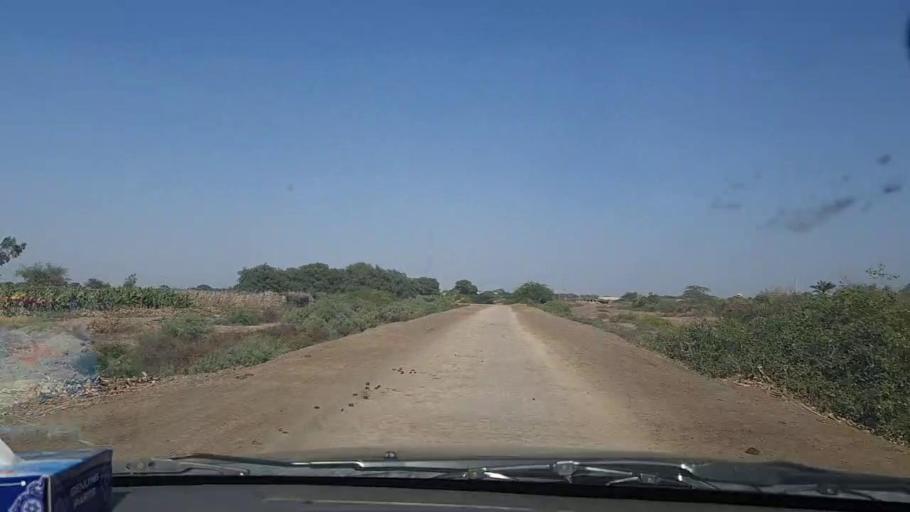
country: PK
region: Sindh
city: Chuhar Jamali
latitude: 24.2902
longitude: 67.7592
